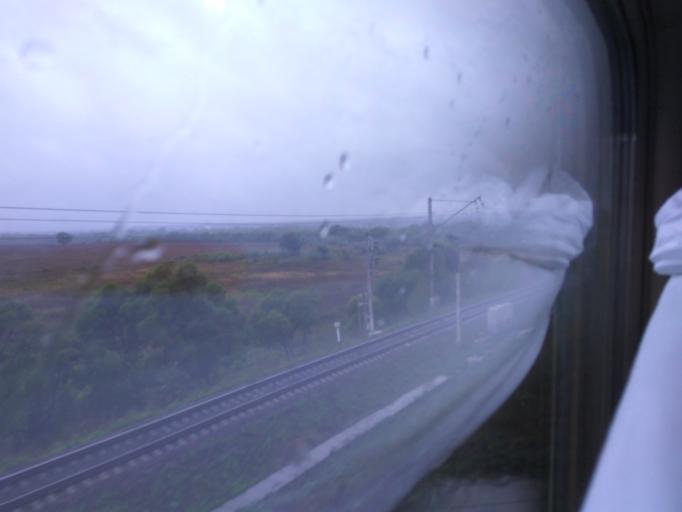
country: RU
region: Moskovskaya
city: Kashira
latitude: 54.8570
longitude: 38.1733
